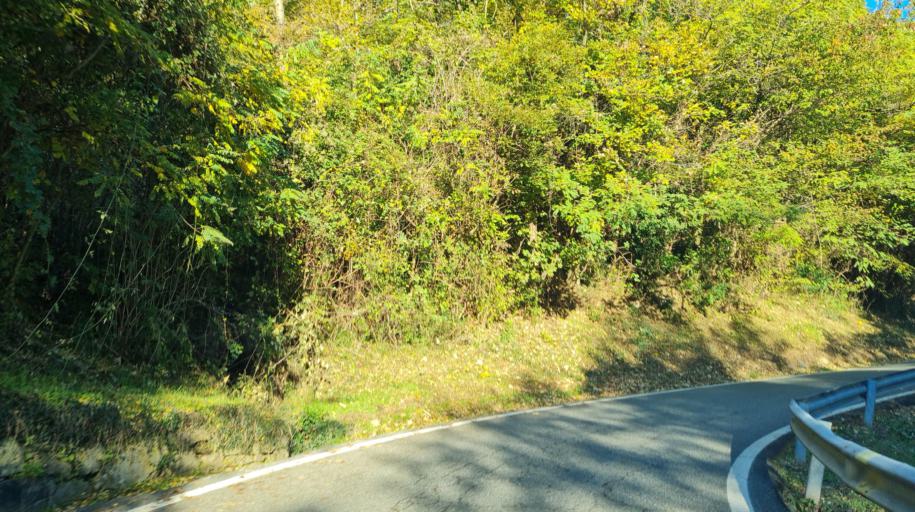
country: IT
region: Piedmont
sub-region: Provincia di Torino
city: Lessolo
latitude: 45.4737
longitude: 7.8055
